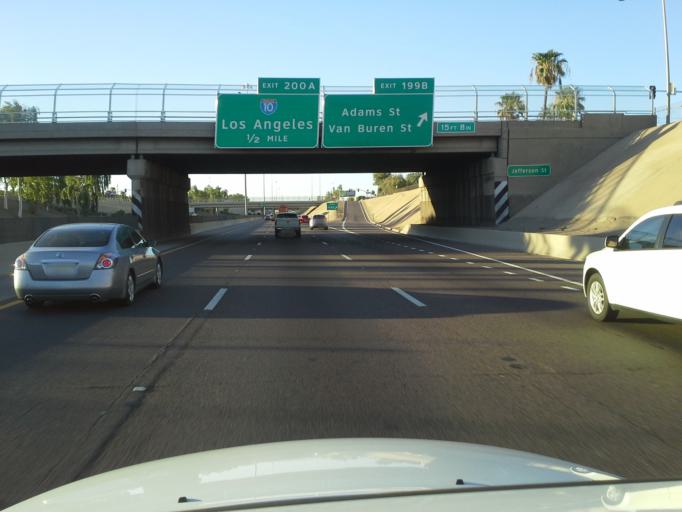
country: US
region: Arizona
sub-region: Maricopa County
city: Phoenix
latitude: 33.4465
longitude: -112.1081
